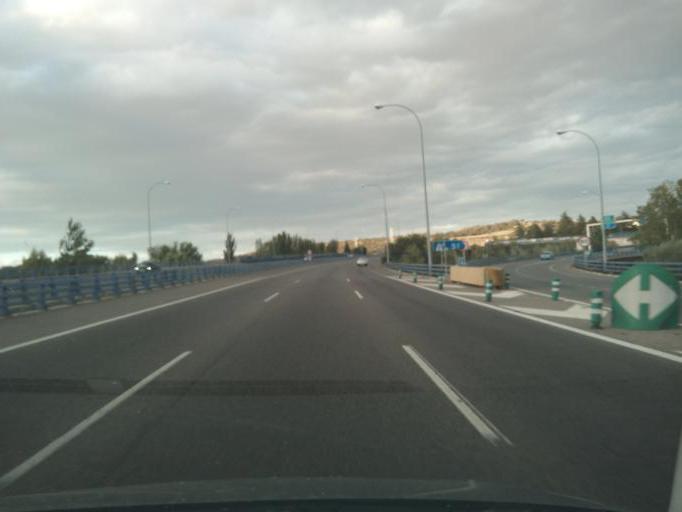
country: ES
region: Madrid
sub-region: Provincia de Madrid
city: Fuencarral-El Pardo
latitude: 40.4758
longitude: -3.7549
